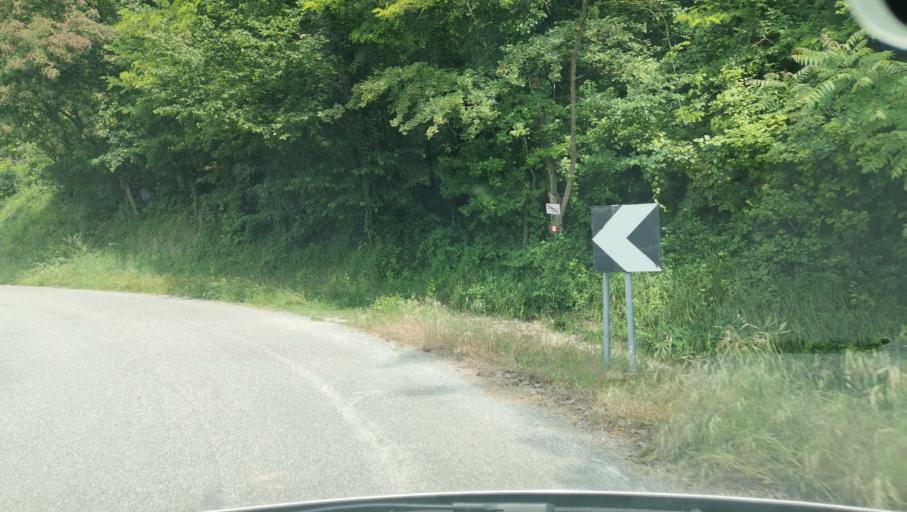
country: IT
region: Piedmont
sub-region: Provincia di Alessandria
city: Odalengo Piccolo
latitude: 45.0753
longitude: 8.1971
